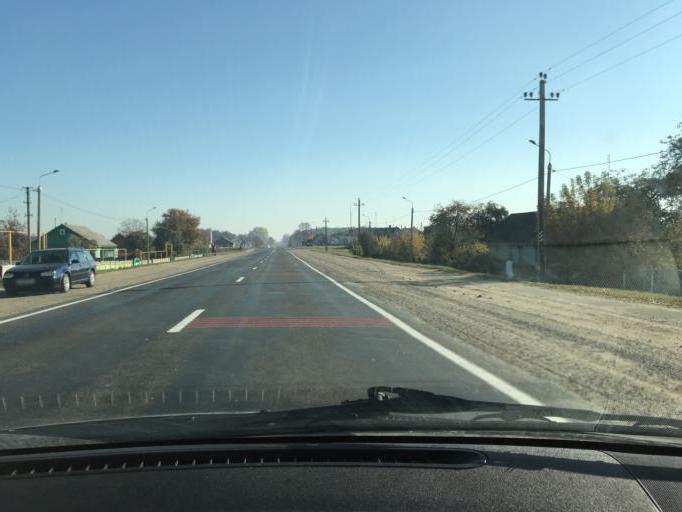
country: BY
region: Minsk
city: Klyetsk
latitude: 52.9629
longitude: 26.4633
